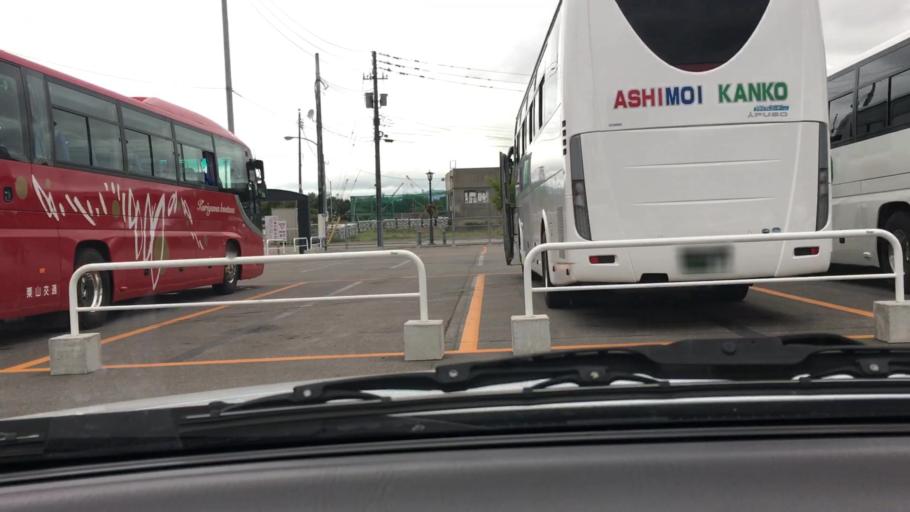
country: JP
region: Hokkaido
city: Hakodate
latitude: 41.7671
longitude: 140.7182
